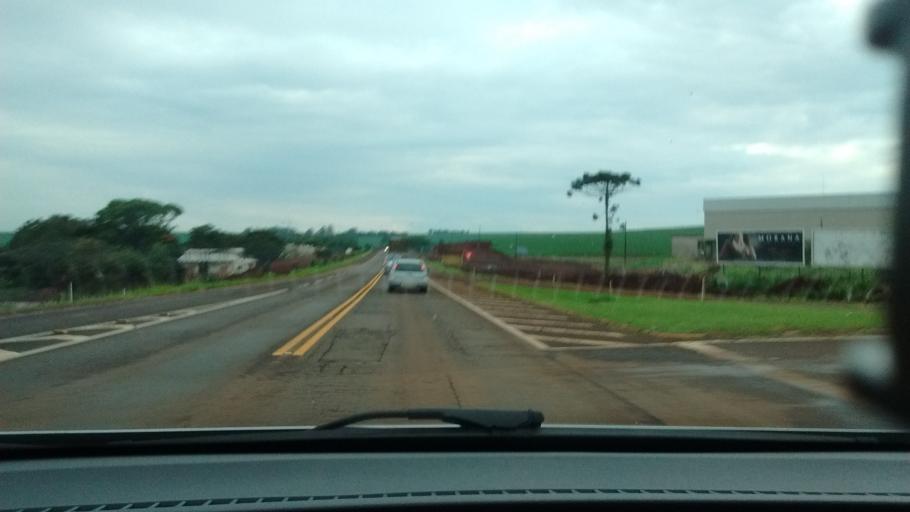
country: BR
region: Parana
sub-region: Corbelia
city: Corbelia
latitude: -24.8024
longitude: -53.2910
